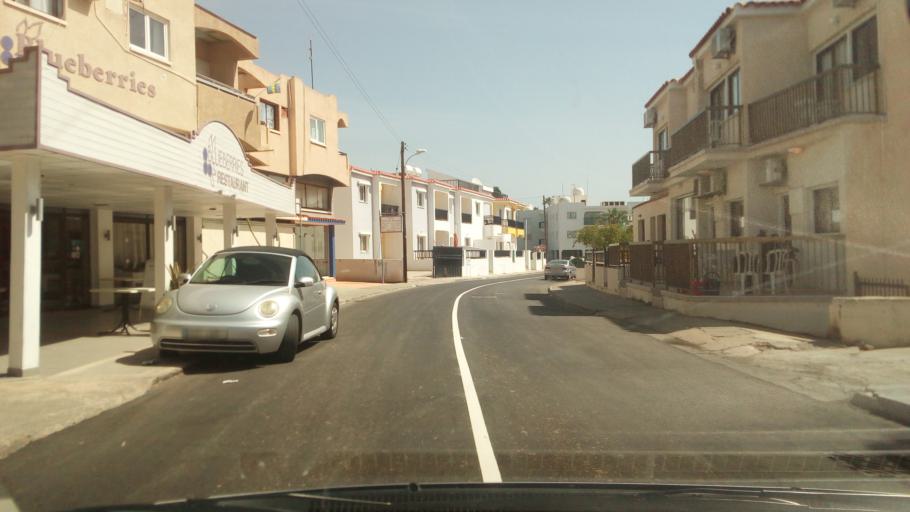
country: CY
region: Ammochostos
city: Ayia Napa
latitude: 34.9887
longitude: 33.9931
